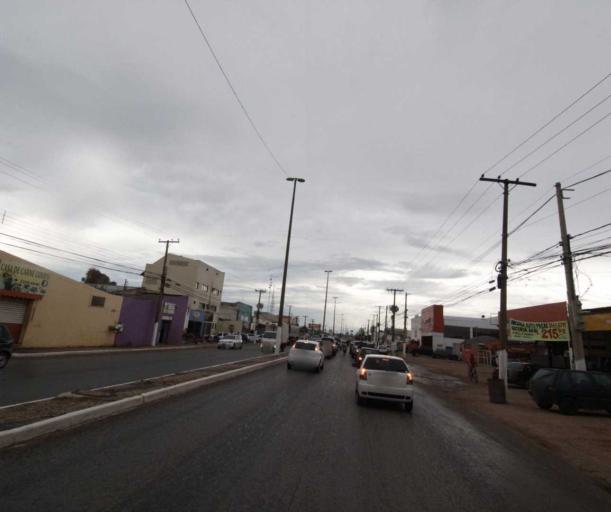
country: BR
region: Mato Grosso
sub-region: Cuiaba
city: Cuiaba
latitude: -15.6332
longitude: -56.0487
